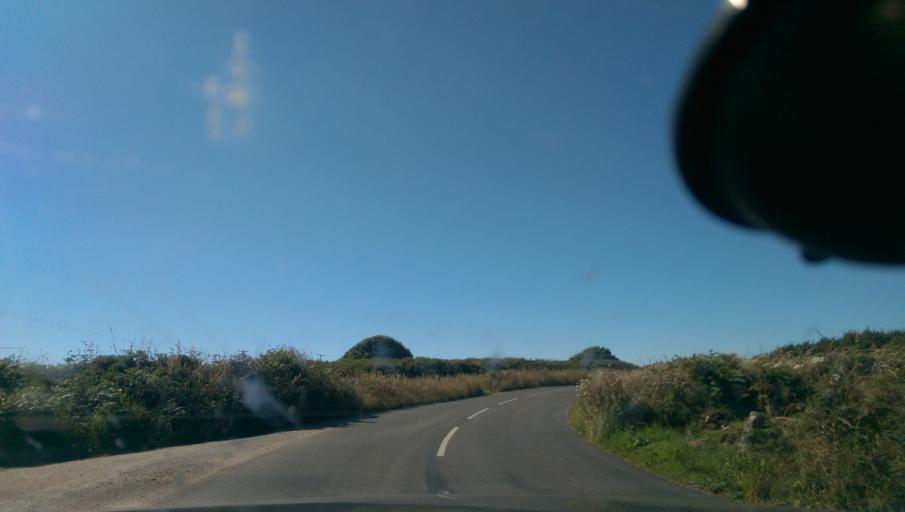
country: GB
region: England
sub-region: Cornwall
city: Sennen
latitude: 50.0641
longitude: -5.6921
